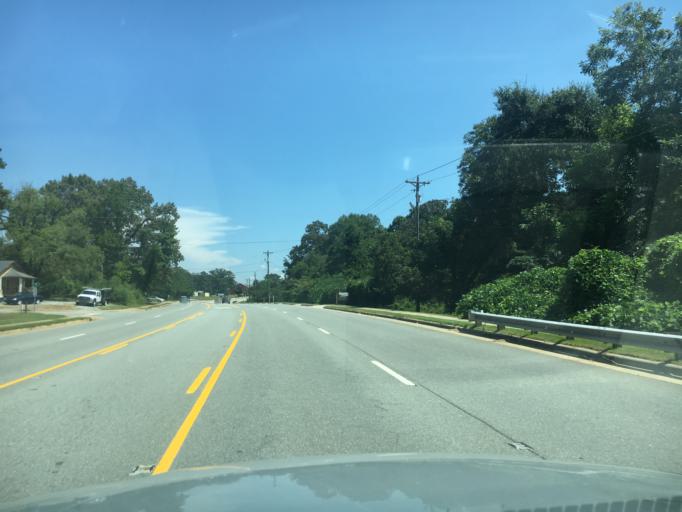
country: US
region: North Carolina
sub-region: Rutherford County
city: Forest City
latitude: 35.3328
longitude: -81.8763
